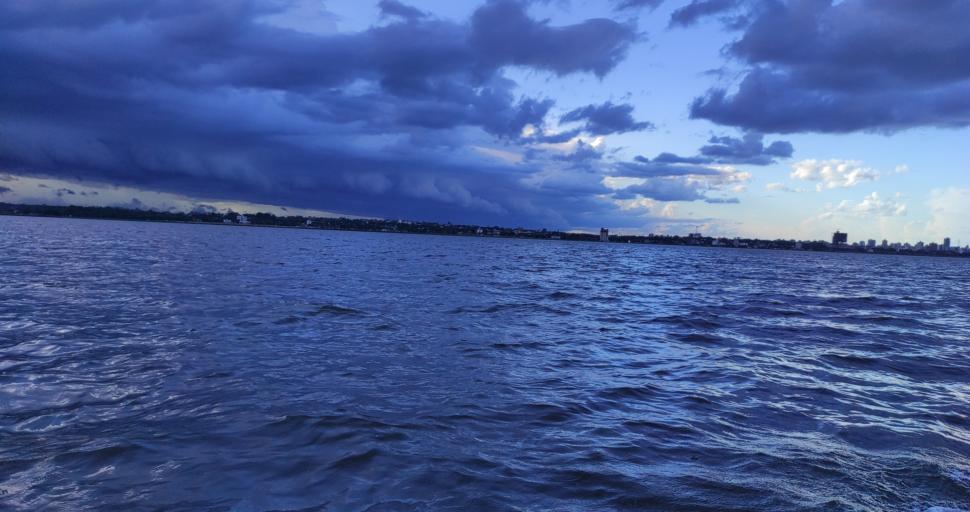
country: AR
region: Misiones
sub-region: Departamento de Capital
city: Posadas
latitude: -27.4104
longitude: -55.8732
